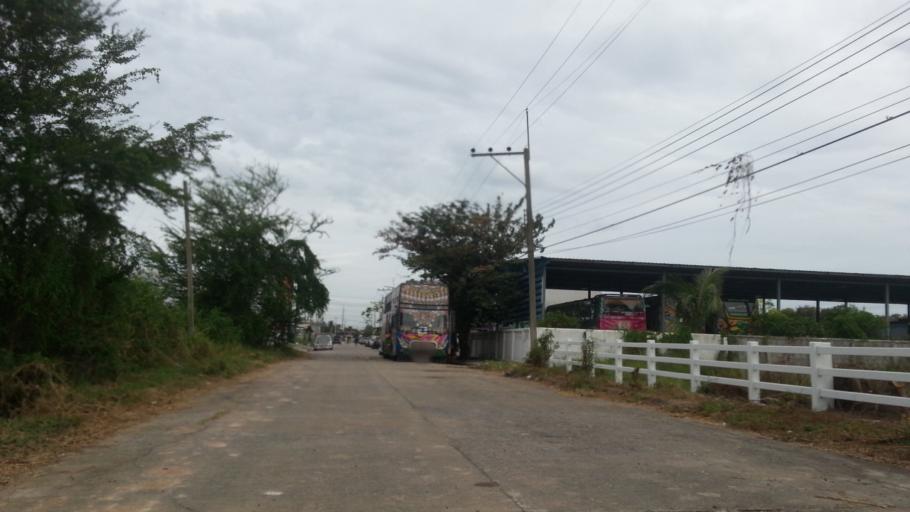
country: TH
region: Pathum Thani
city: Nong Suea
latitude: 14.0681
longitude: 100.8786
